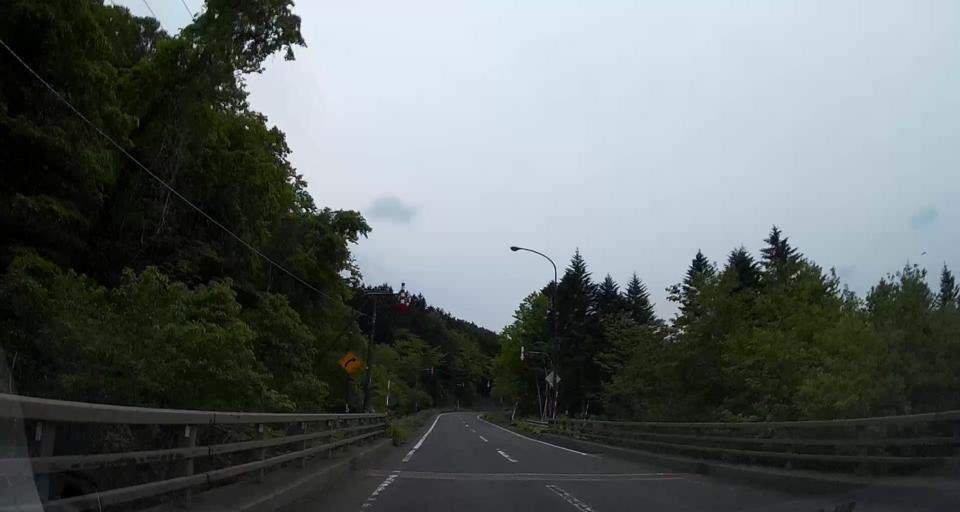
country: JP
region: Hokkaido
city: Shiraoi
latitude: 42.6499
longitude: 141.2007
